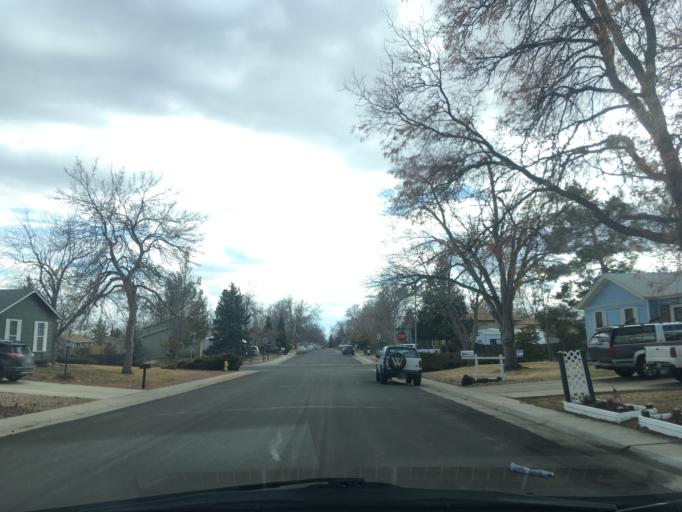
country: US
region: Colorado
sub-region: Broomfield County
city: Broomfield
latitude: 39.9417
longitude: -105.0550
